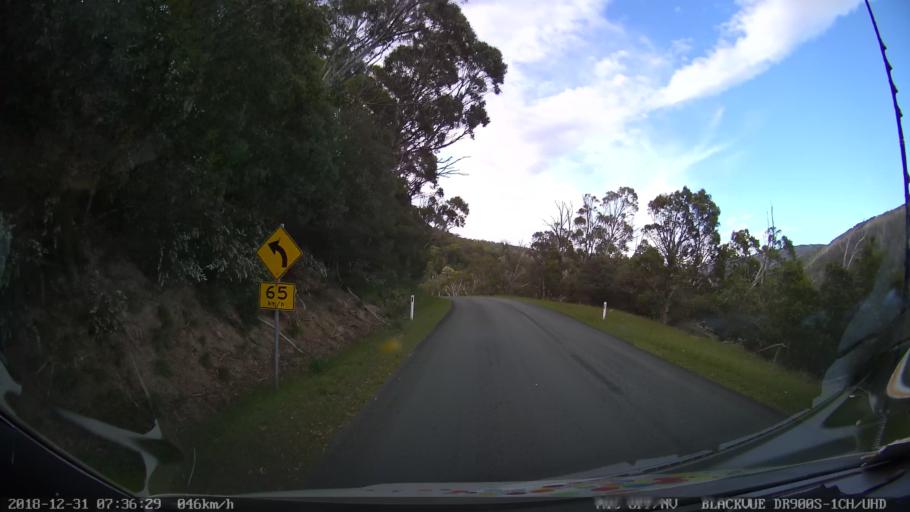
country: AU
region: New South Wales
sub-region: Snowy River
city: Jindabyne
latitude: -36.3412
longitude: 148.4425
